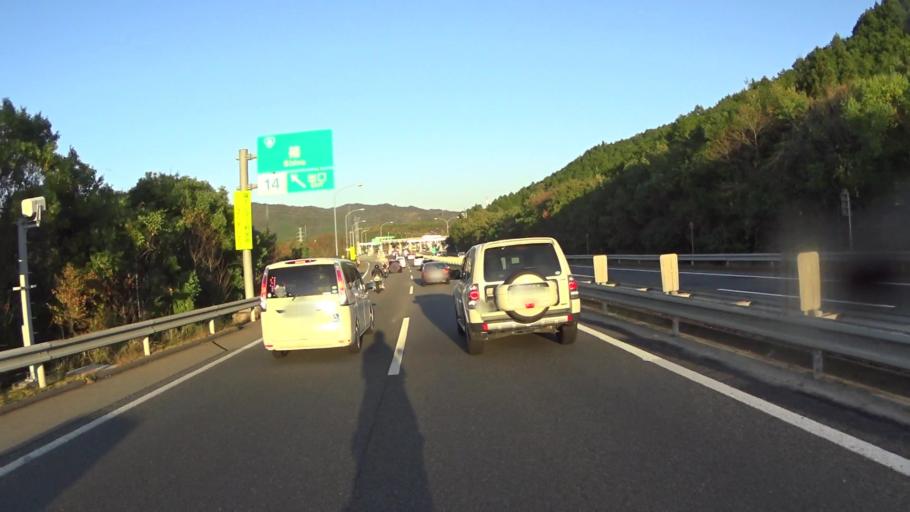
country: JP
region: Kyoto
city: Kameoka
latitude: 34.9893
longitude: 135.6034
